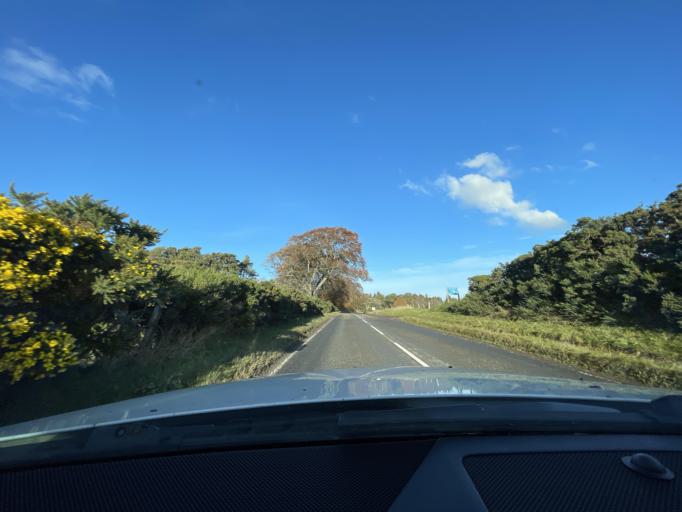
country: GB
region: Scotland
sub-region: Highland
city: Inverness
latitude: 57.3890
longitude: -4.3281
